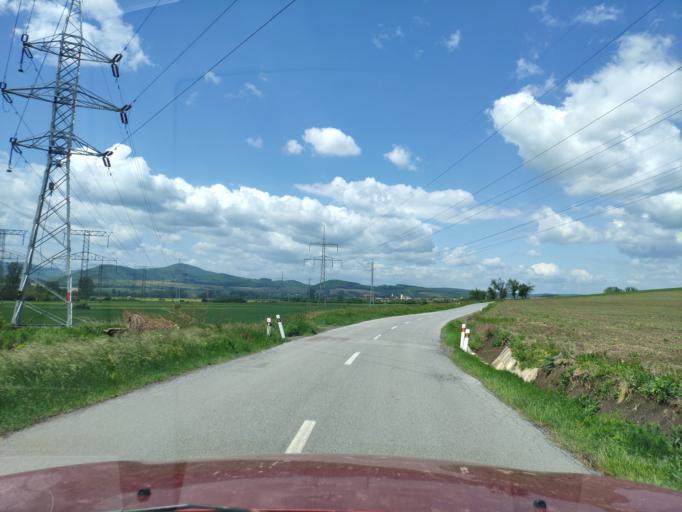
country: SK
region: Presovsky
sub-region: Okres Presov
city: Presov
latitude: 48.8605
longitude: 21.2943
